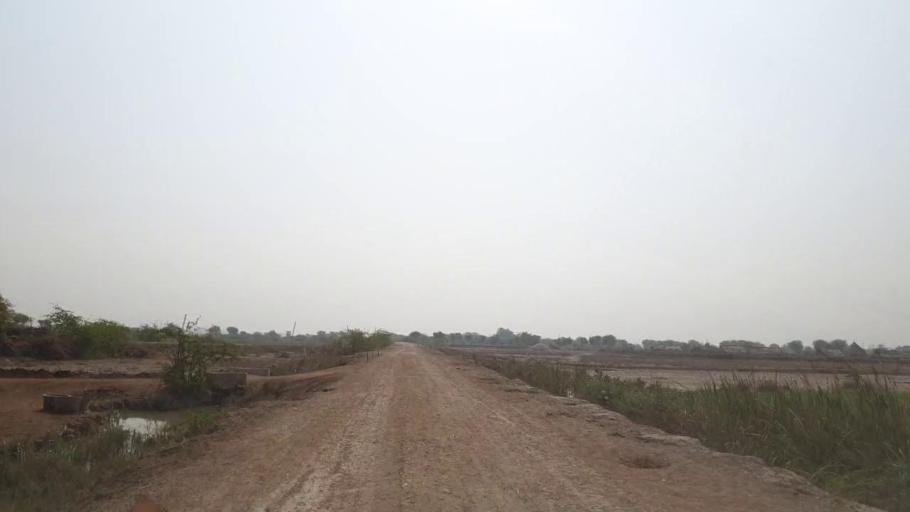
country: PK
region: Sindh
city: Mirpur Khas
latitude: 25.5381
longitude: 69.0625
